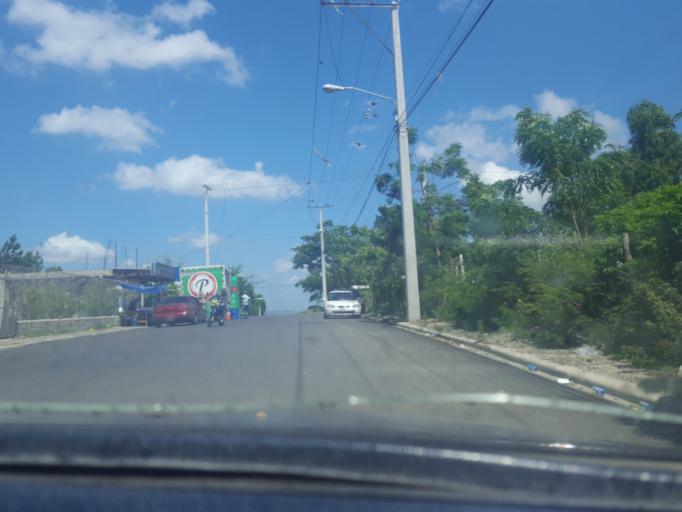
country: DO
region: Santiago
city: Santiago de los Caballeros
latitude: 19.4904
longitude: -70.6964
